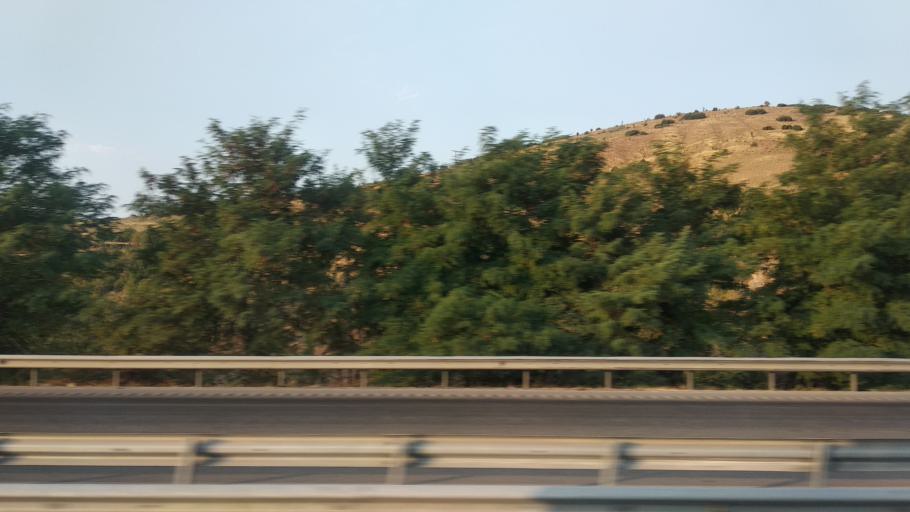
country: TR
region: Manisa
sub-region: Kula
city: Kula
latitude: 38.5663
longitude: 28.5836
